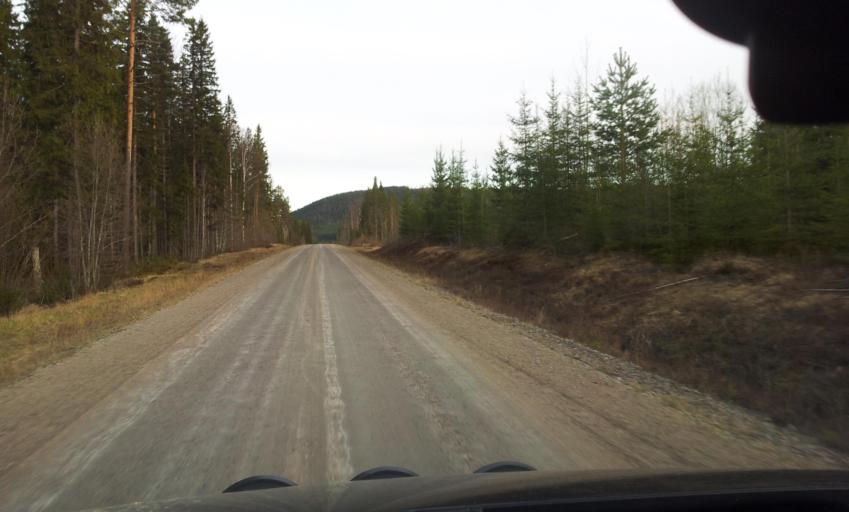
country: SE
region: Gaevleborg
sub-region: Ljusdals Kommun
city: Farila
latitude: 62.0773
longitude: 15.7752
